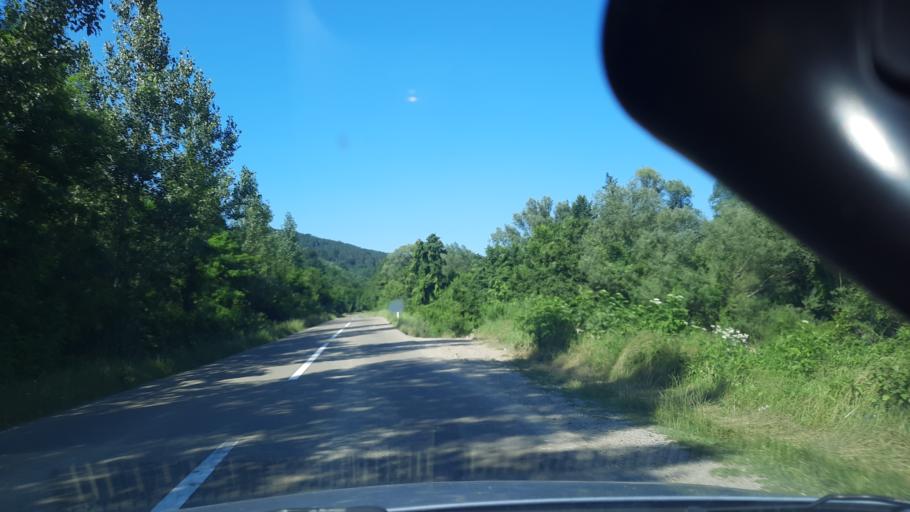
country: RS
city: Turija
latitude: 44.5219
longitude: 21.6072
